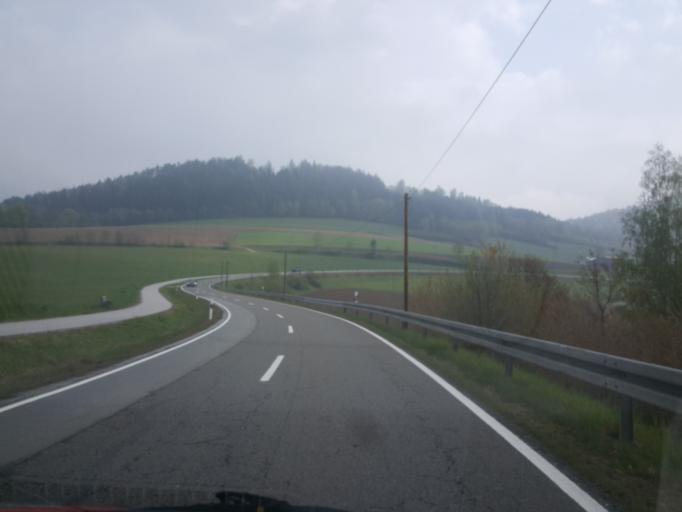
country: DE
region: Bavaria
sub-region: Lower Bavaria
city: Geiersthal
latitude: 49.0547
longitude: 12.9576
